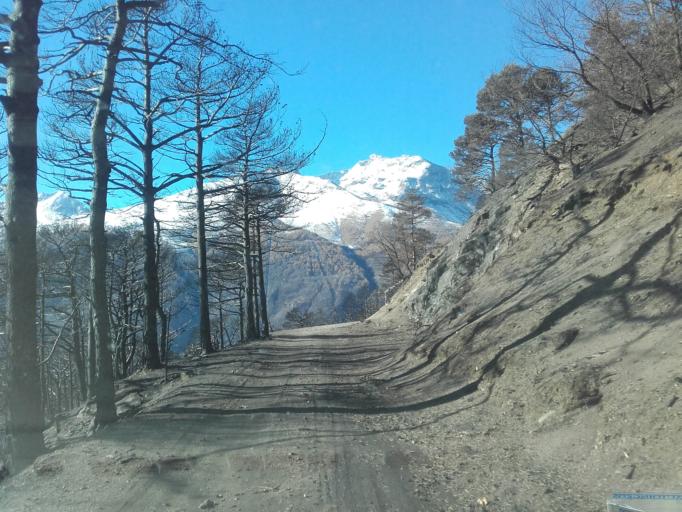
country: IT
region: Piedmont
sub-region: Provincia di Torino
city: Mompantero
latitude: 45.1607
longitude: 7.0296
